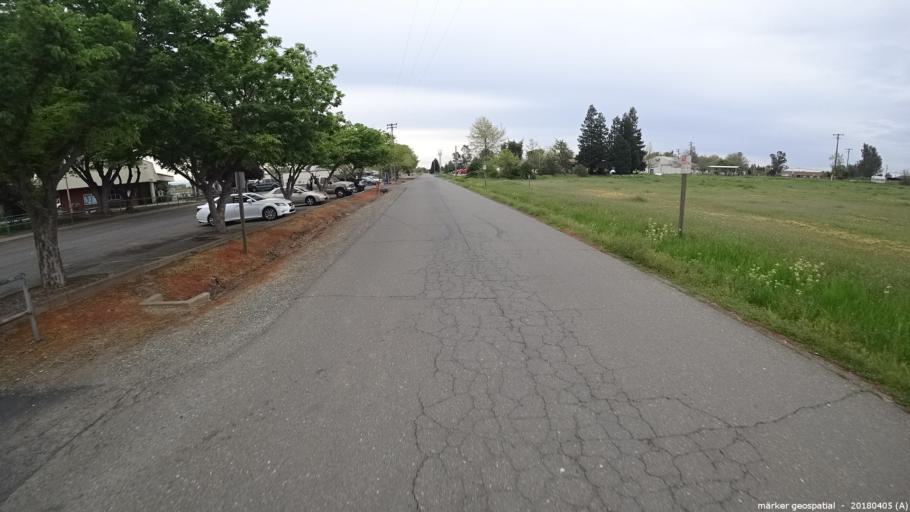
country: US
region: California
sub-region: Sacramento County
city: Herald
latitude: 38.2950
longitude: -121.2426
